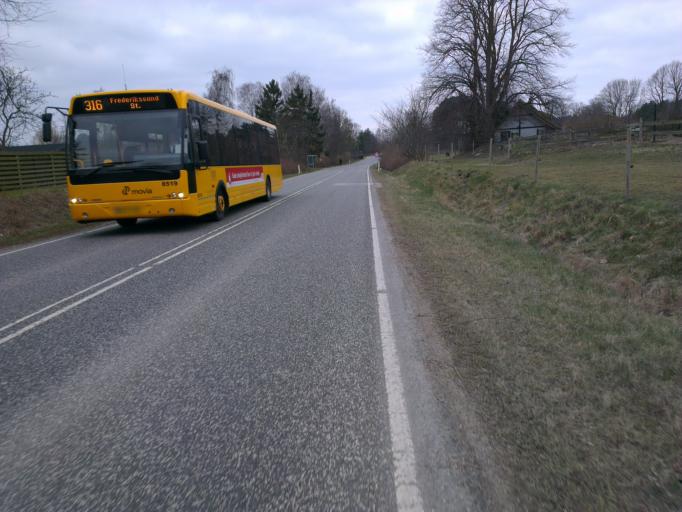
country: DK
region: Capital Region
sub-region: Frederikssund Kommune
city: Jaegerspris
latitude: 55.9047
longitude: 11.9408
